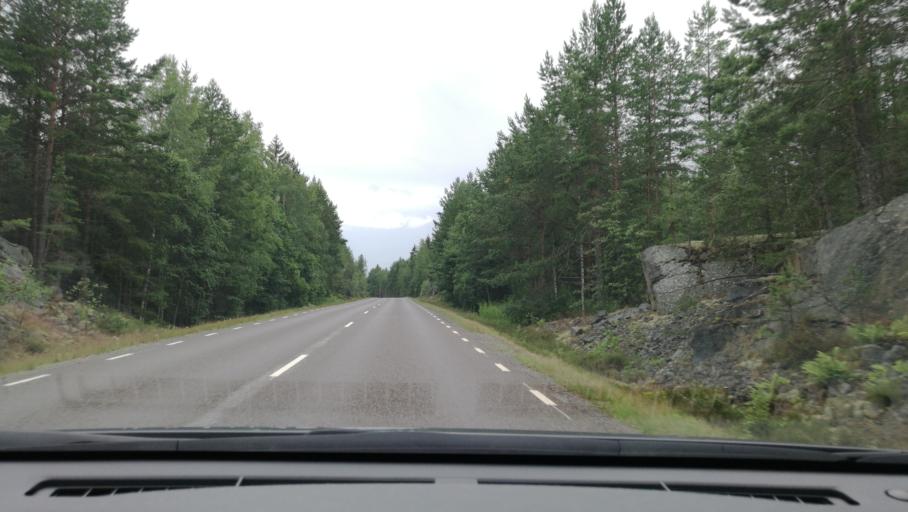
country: SE
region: OEstergoetland
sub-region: Norrkopings Kommun
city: Svartinge
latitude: 58.8123
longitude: 15.9410
